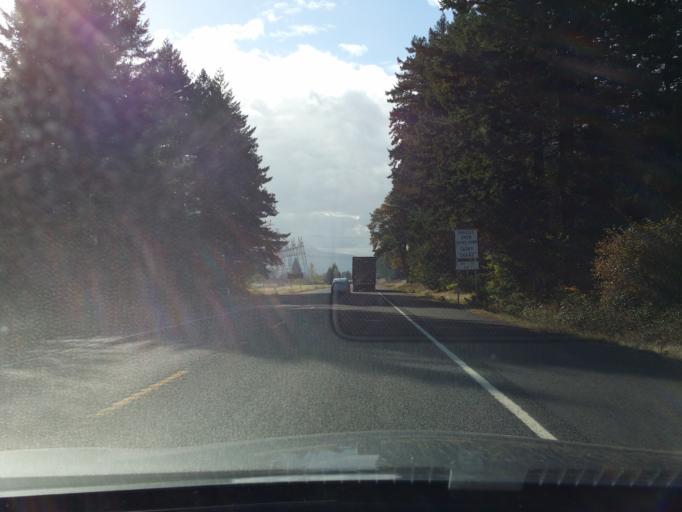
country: US
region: Oregon
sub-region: Hood River County
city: Cascade Locks
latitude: 45.6492
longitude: -121.9498
